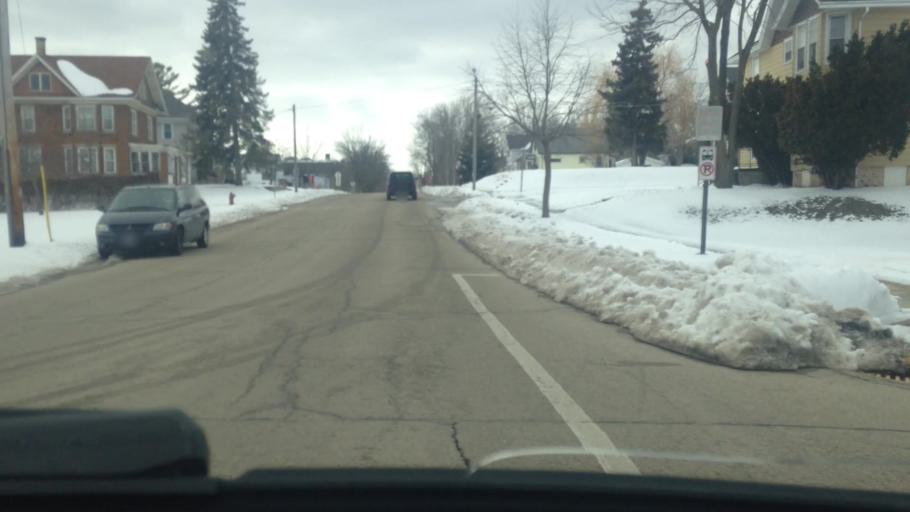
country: US
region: Wisconsin
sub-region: Dodge County
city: Mayville
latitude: 43.4956
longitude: -88.5506
